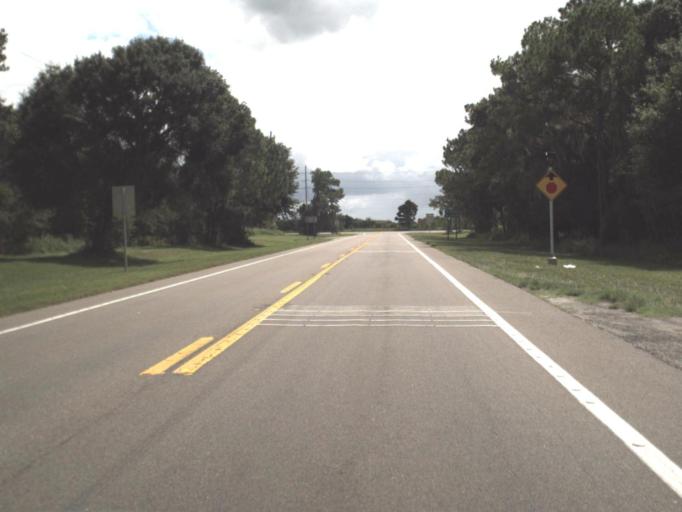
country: US
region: Florida
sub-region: Polk County
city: Mulberry
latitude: 27.7047
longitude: -82.0228
